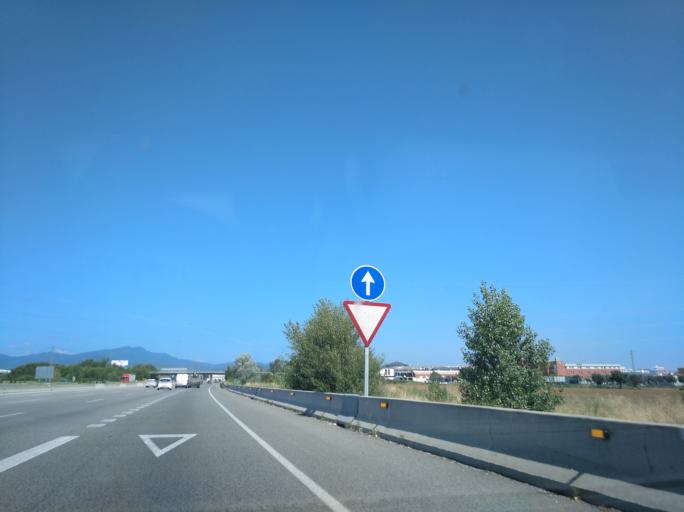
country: ES
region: Catalonia
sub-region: Provincia de Girona
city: Vilablareix
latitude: 41.9617
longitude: 2.7822
